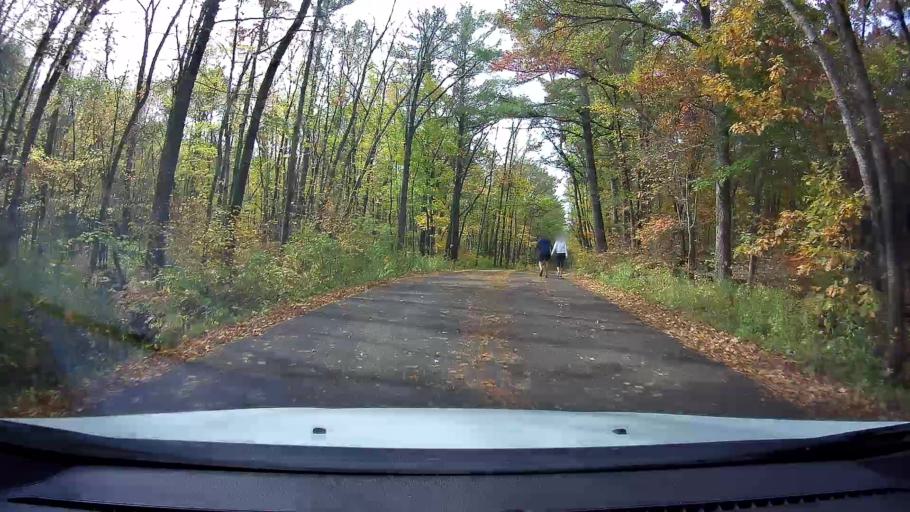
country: US
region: Wisconsin
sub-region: Polk County
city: Saint Croix Falls
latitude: 45.3909
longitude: -92.6525
